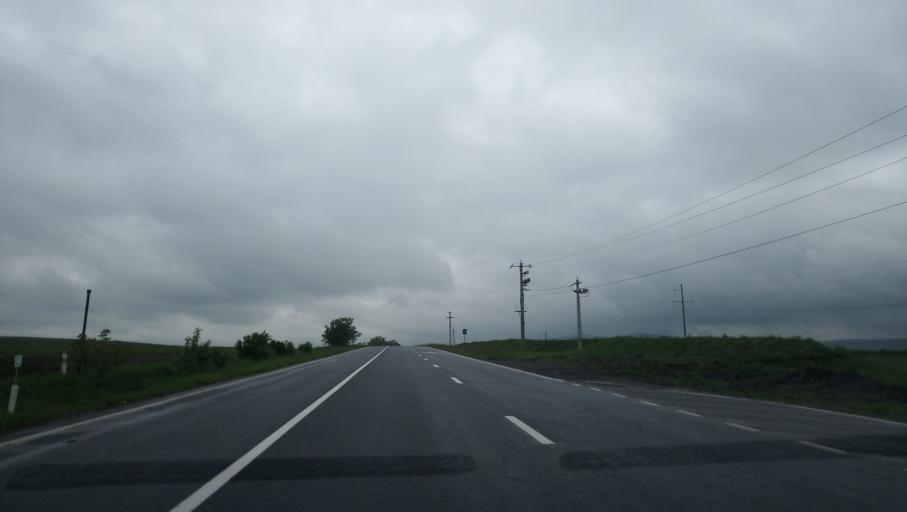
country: RO
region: Alba
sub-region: Comuna Cut
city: Cut
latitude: 45.9181
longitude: 23.7059
